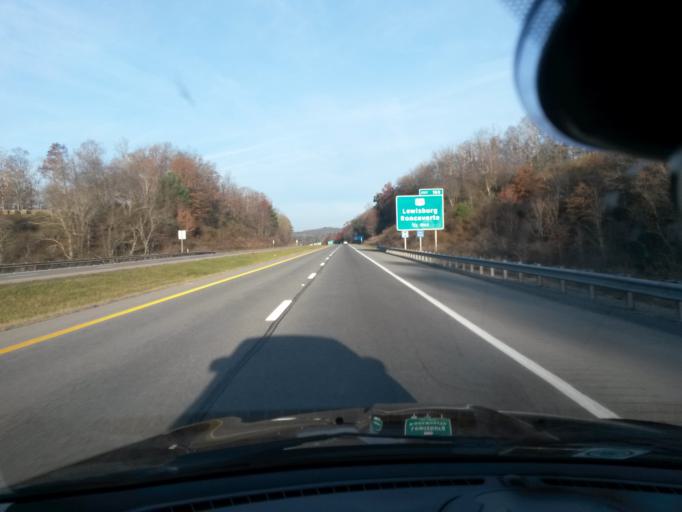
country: US
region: West Virginia
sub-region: Greenbrier County
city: Lewisburg
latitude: 37.8106
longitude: -80.4163
